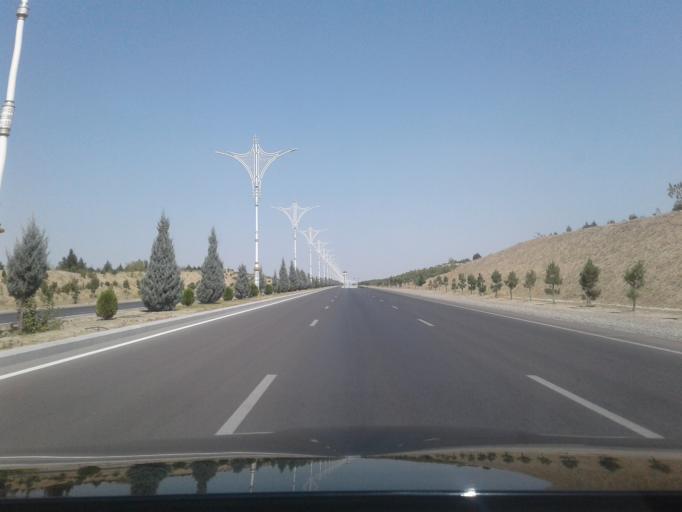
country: TM
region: Ahal
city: Ashgabat
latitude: 37.8783
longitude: 58.4040
